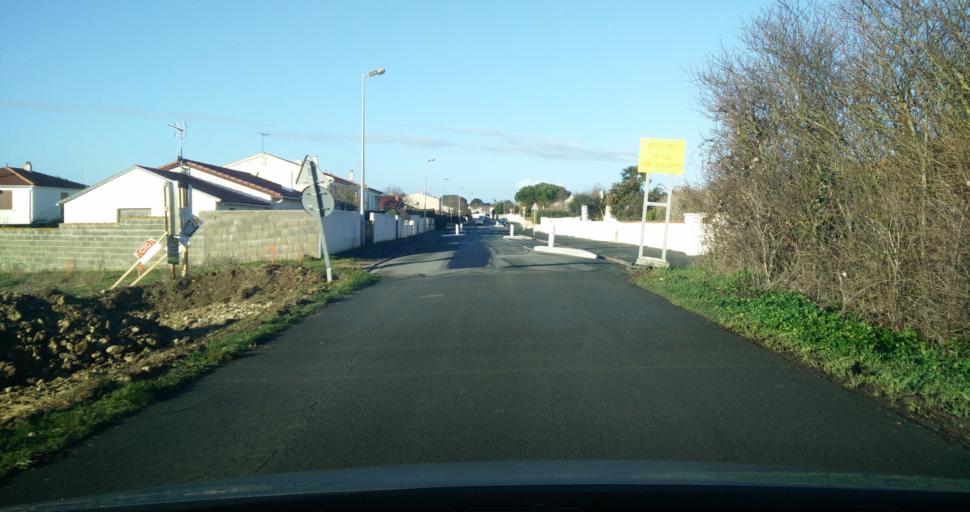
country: FR
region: Poitou-Charentes
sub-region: Departement de la Charente-Maritime
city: Saint-Xandre
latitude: 46.2038
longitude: -1.0947
